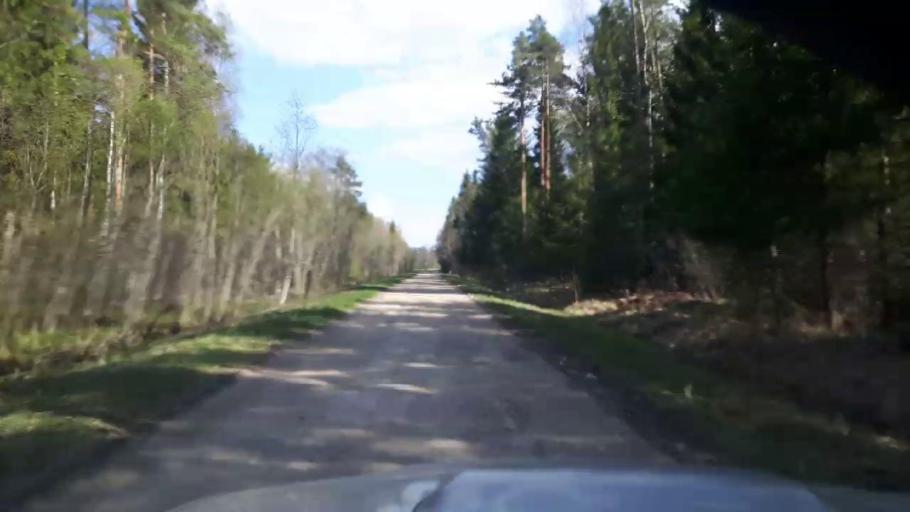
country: EE
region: Paernumaa
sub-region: Tootsi vald
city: Tootsi
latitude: 58.4446
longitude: 24.8731
